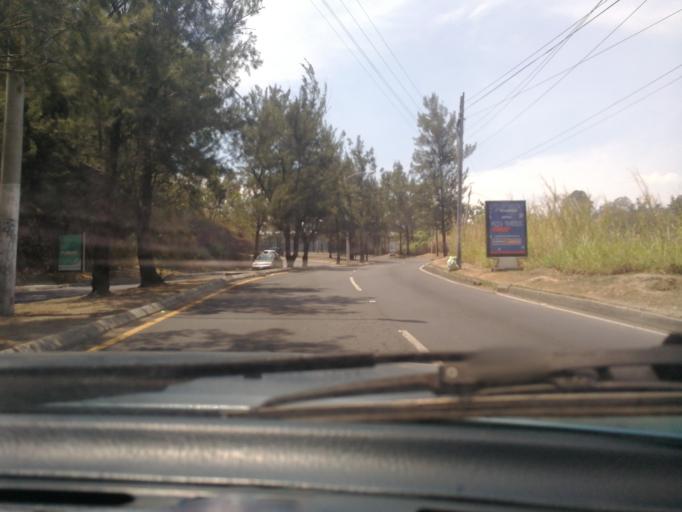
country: GT
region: Guatemala
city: Guatemala City
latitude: 14.6273
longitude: -90.4828
